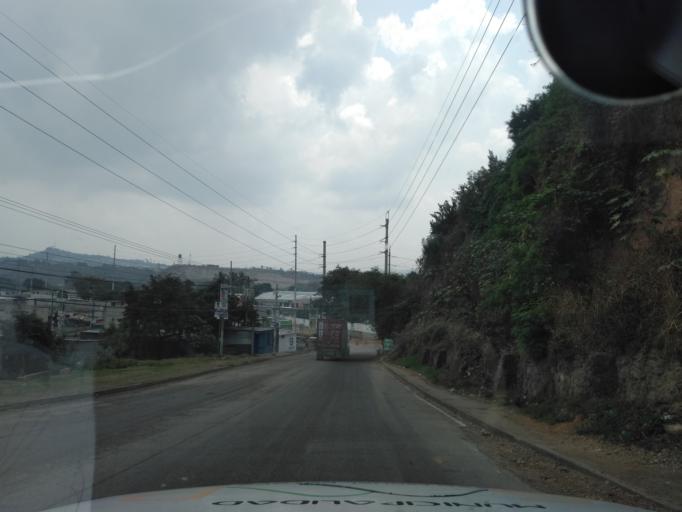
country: GT
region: Guatemala
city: Petapa
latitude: 14.5090
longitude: -90.5587
